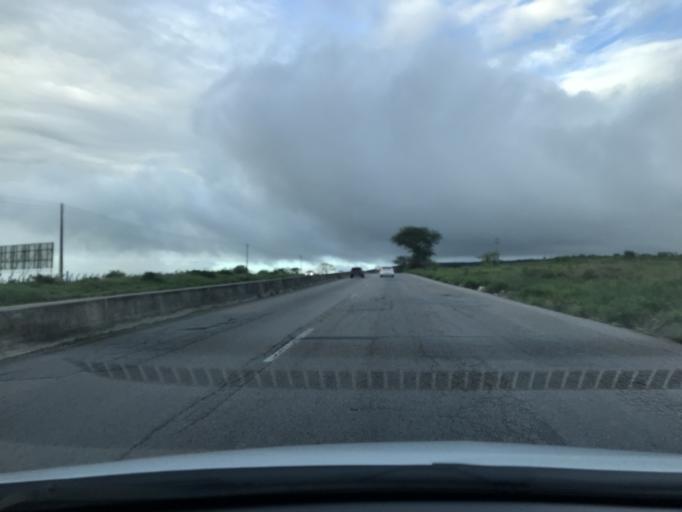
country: BR
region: Pernambuco
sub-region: Bezerros
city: Bezerros
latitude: -8.2980
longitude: -35.8341
